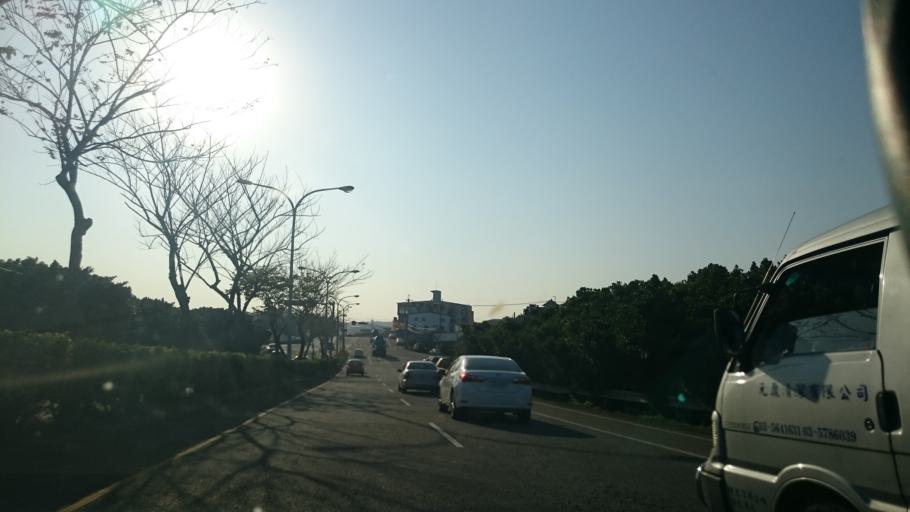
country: TW
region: Taiwan
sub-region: Miaoli
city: Miaoli
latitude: 24.6623
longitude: 120.8797
